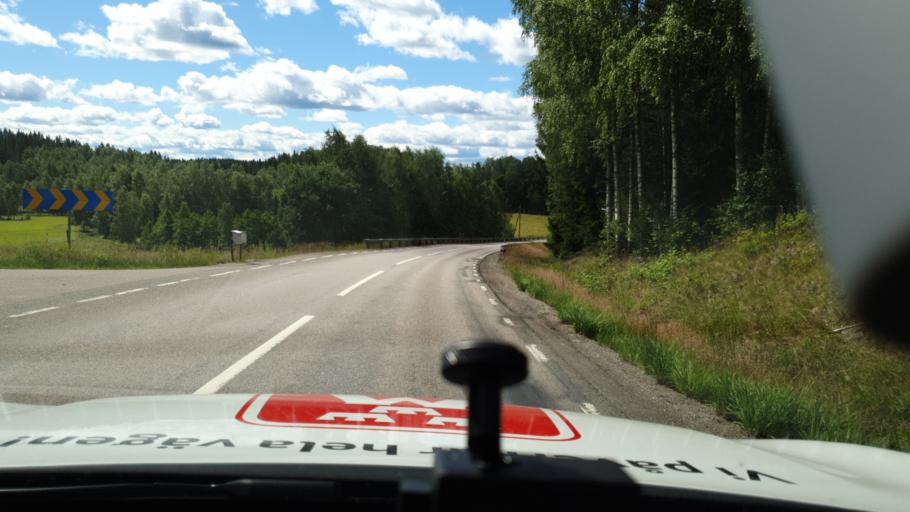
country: SE
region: Vaermland
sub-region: Sunne Kommun
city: Sunne
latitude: 59.6776
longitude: 13.0374
